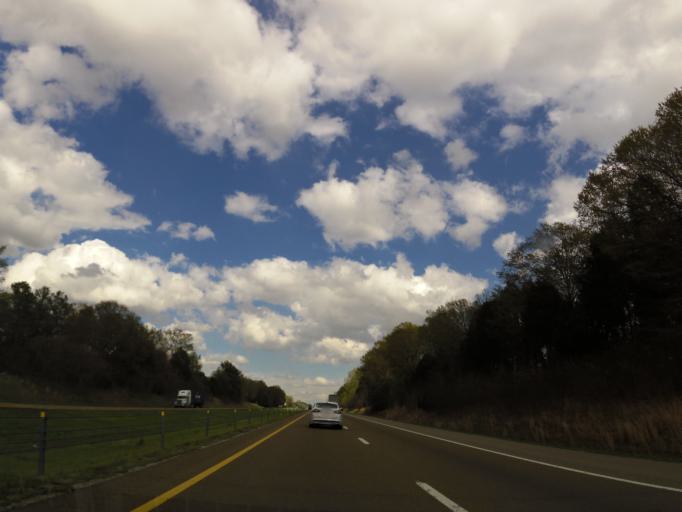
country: US
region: Tennessee
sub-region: Crockett County
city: Bells
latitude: 35.6124
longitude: -89.0145
